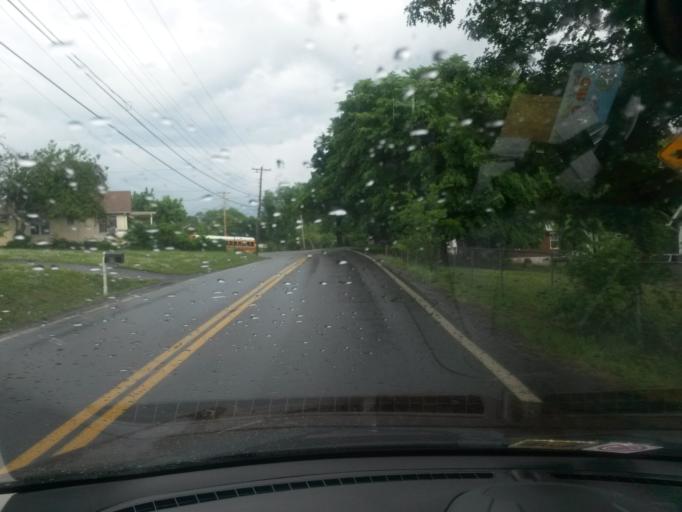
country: US
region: Virginia
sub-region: City of Salem
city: Salem
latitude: 37.3023
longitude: -79.9998
